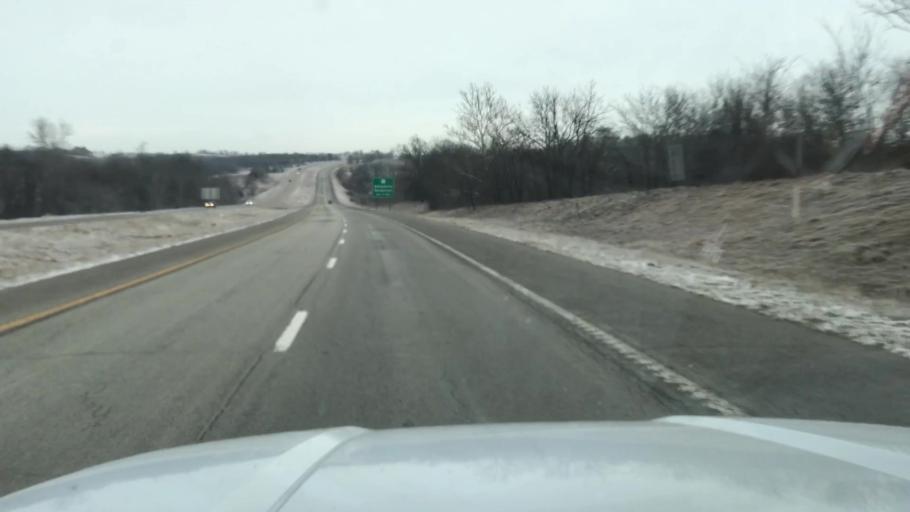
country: US
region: Missouri
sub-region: Andrew County
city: Savannah
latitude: 39.9027
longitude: -94.8574
